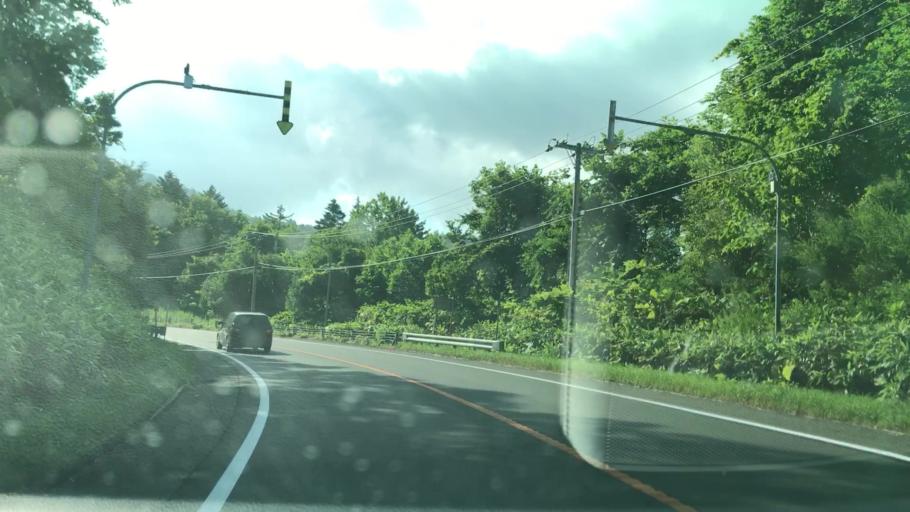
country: JP
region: Hokkaido
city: Shimo-furano
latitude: 42.9088
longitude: 142.4169
